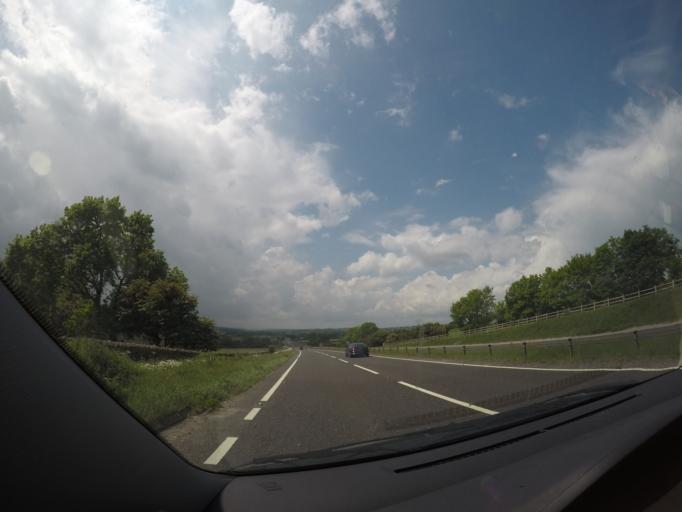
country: GB
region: England
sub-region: County Durham
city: Lartington
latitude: 54.5184
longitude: -1.9734
